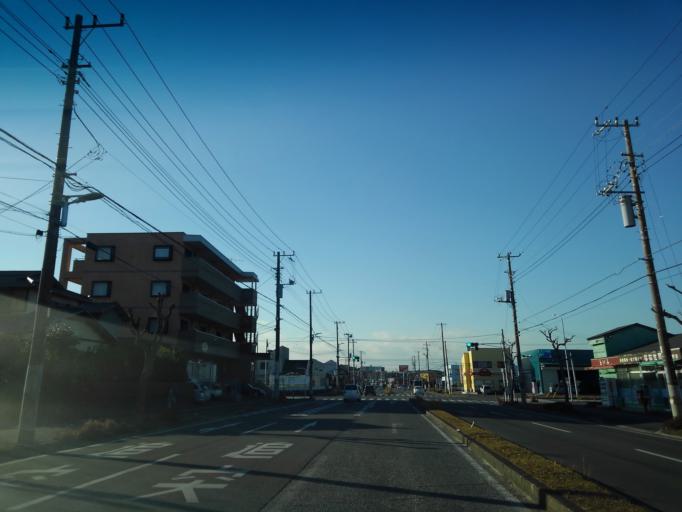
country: JP
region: Chiba
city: Kimitsu
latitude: 35.3319
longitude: 139.8894
